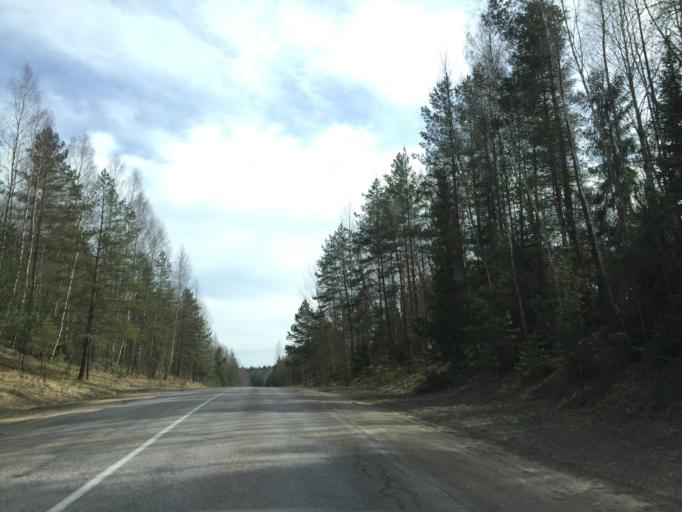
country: LV
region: Ogre
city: Ogre
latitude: 56.8440
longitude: 24.5738
